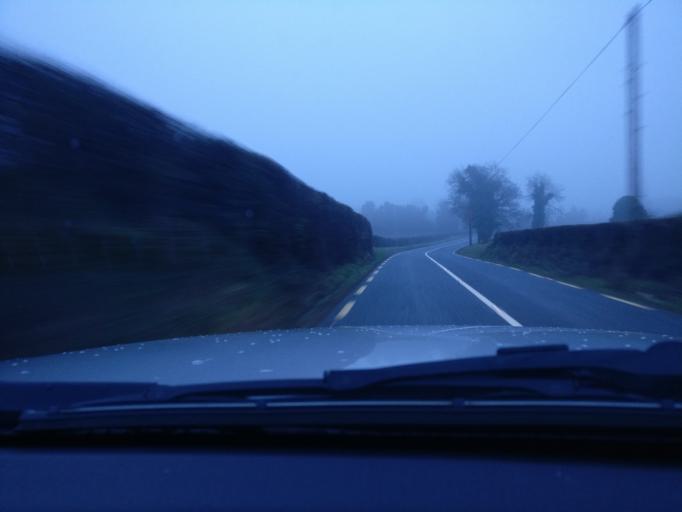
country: IE
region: Leinster
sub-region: An Mhi
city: Ballivor
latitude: 53.6086
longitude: -7.0055
